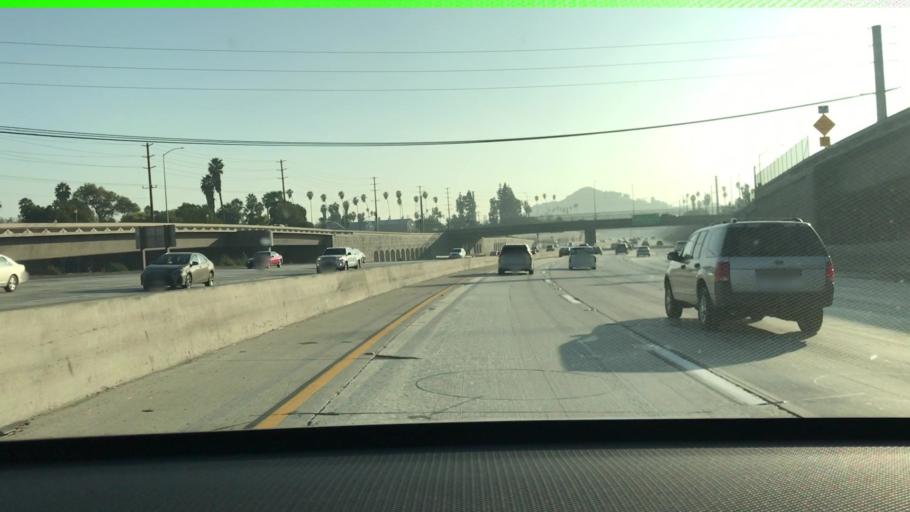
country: US
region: California
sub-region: Riverside County
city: Riverside
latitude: 33.9758
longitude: -117.3721
